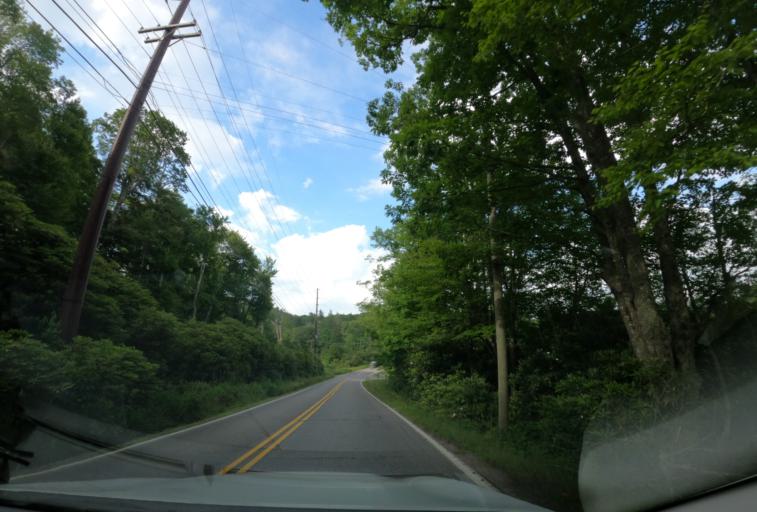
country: US
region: North Carolina
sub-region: Jackson County
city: Cullowhee
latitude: 35.0878
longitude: -83.1736
